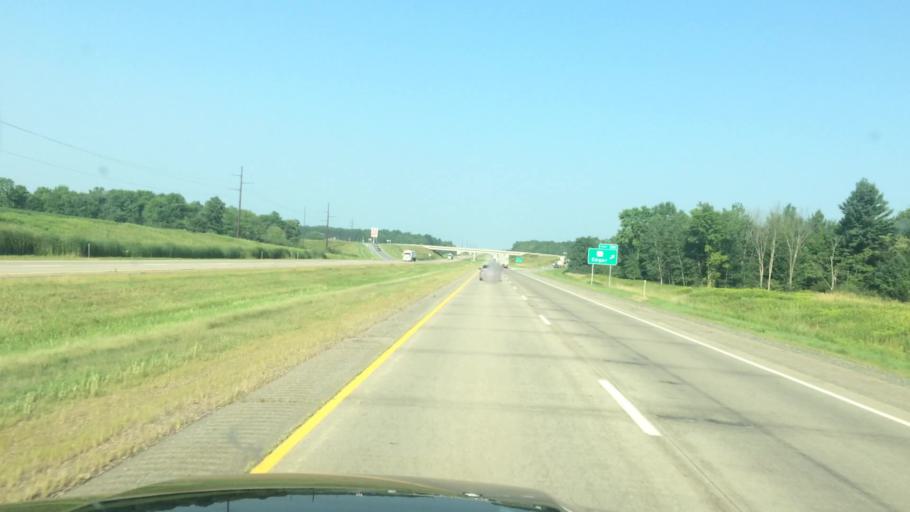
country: US
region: Wisconsin
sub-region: Marathon County
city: Edgar
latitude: 44.9446
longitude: -89.9561
